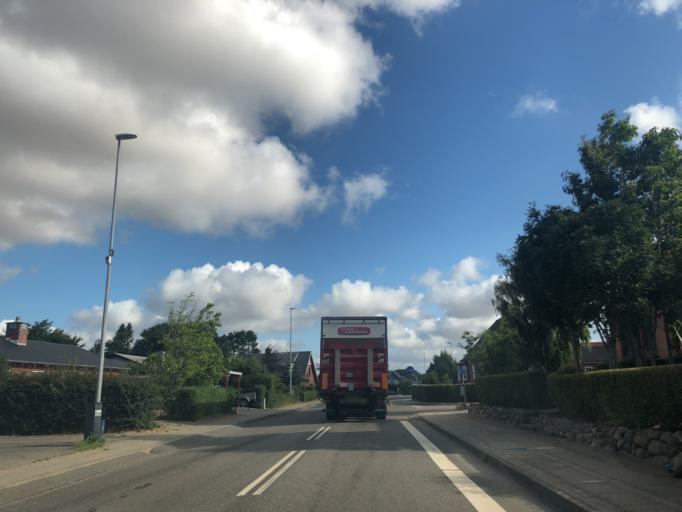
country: DK
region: Central Jutland
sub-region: Skive Kommune
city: Skive
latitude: 56.6526
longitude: 8.9331
